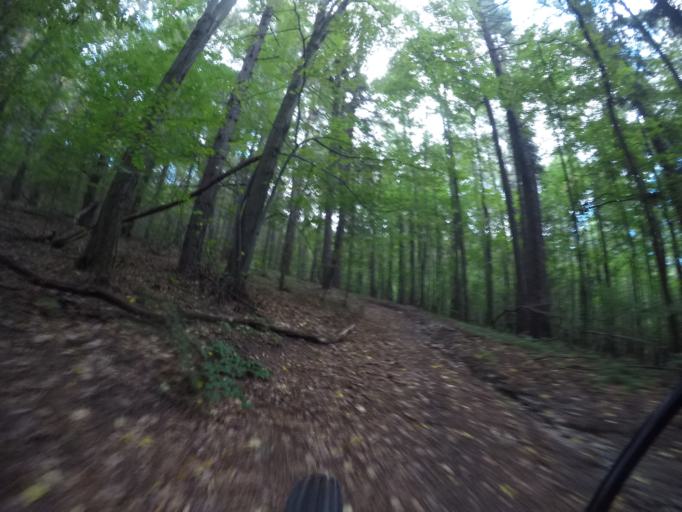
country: SK
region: Kosicky
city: Gelnica
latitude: 48.9244
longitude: 21.0299
